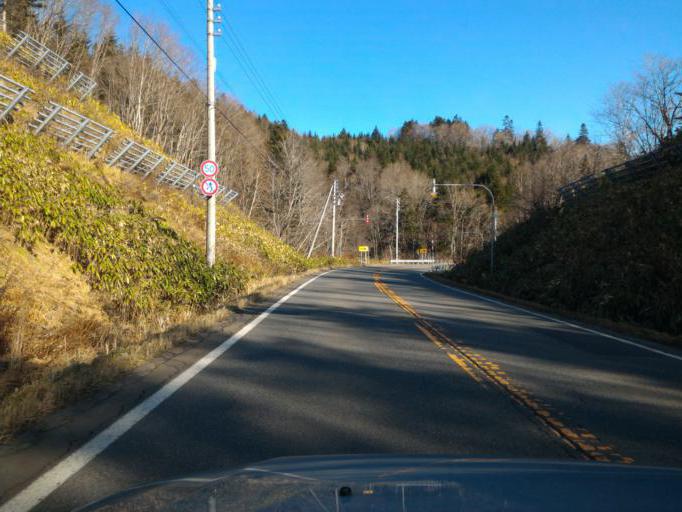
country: JP
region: Hokkaido
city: Bibai
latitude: 43.2784
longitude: 142.0555
